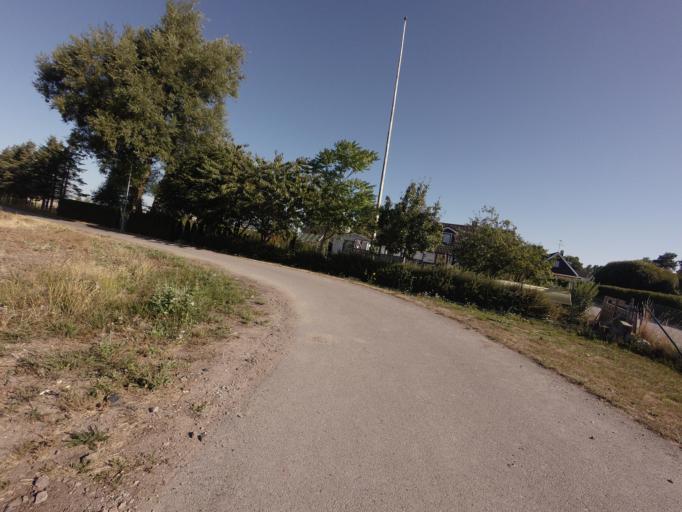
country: SE
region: Skane
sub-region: Trelleborgs Kommun
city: Skare
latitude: 55.4037
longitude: 13.0915
